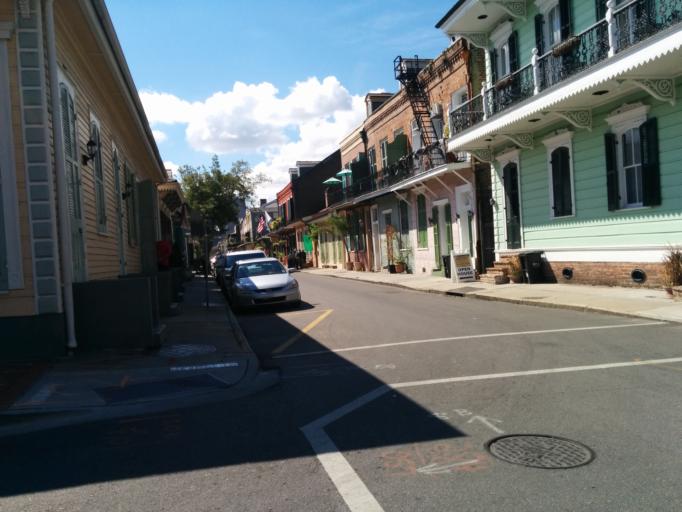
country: US
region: Louisiana
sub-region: Orleans Parish
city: New Orleans
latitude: 29.9623
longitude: -90.0652
